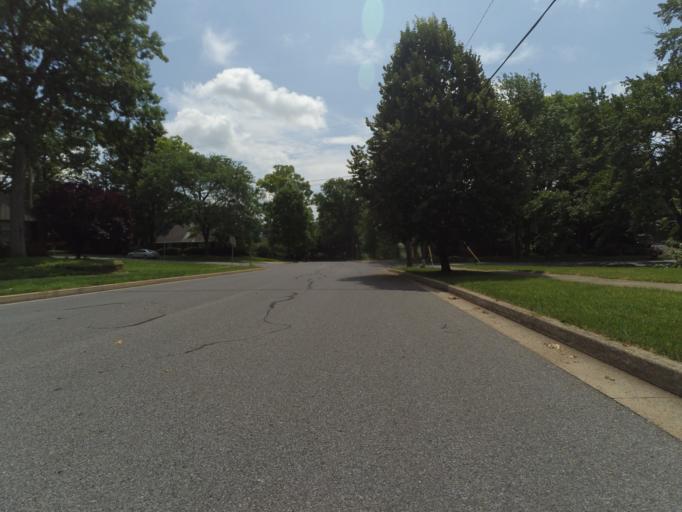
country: US
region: Pennsylvania
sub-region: Centre County
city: State College
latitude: 40.7880
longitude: -77.8408
